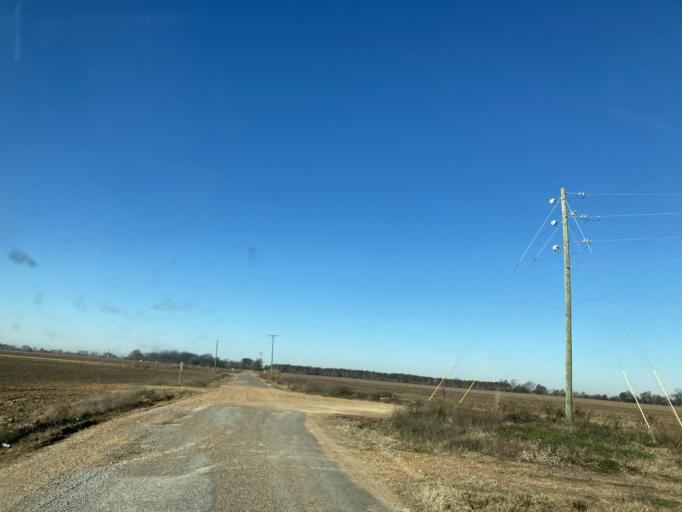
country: US
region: Mississippi
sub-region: Yazoo County
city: Yazoo City
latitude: 32.9226
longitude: -90.5919
